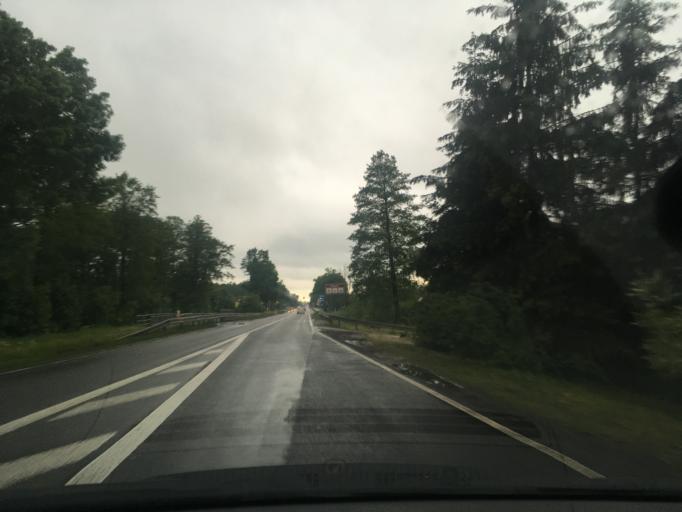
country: PL
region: Lublin Voivodeship
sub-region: Powiat rycki
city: Deblin
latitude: 51.5719
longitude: 21.8920
